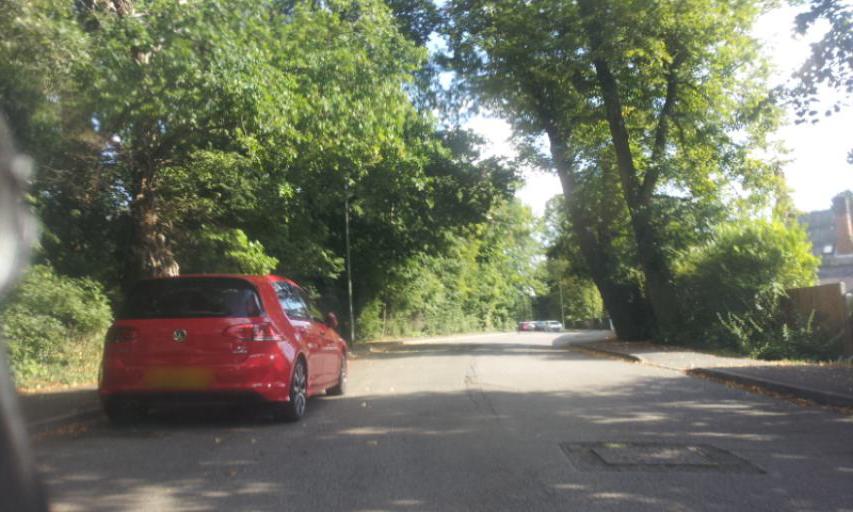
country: GB
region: England
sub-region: Greater London
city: Chislehurst
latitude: 51.3977
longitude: 0.0589
